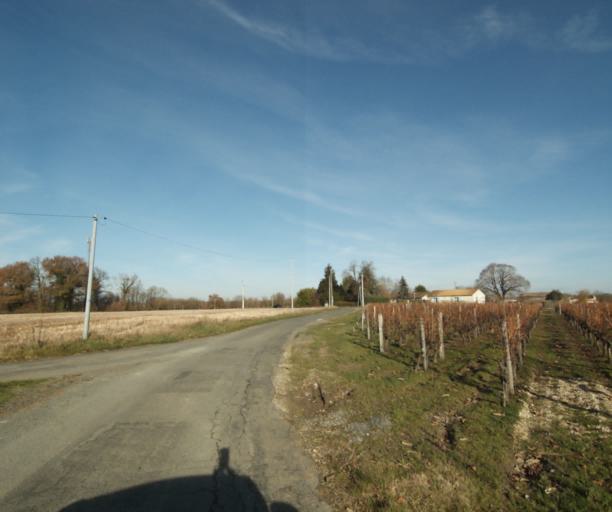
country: FR
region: Poitou-Charentes
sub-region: Departement de la Charente-Maritime
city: Ecoyeux
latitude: 45.7575
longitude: -0.4951
